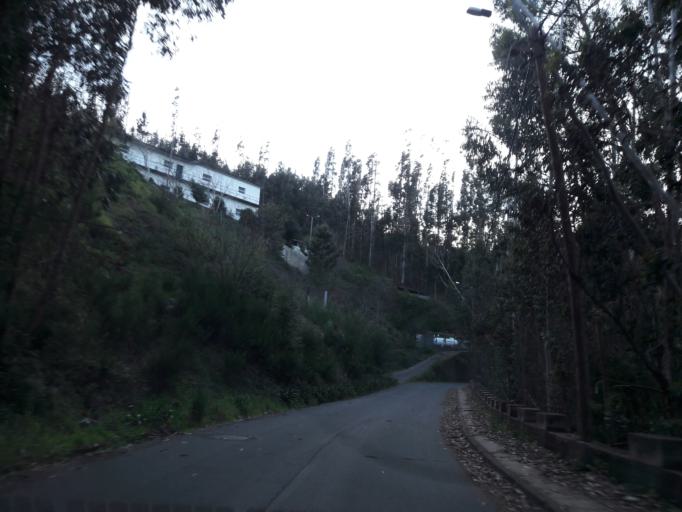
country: PT
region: Madeira
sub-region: Santa Cruz
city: Camacha
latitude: 32.6889
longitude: -16.8642
